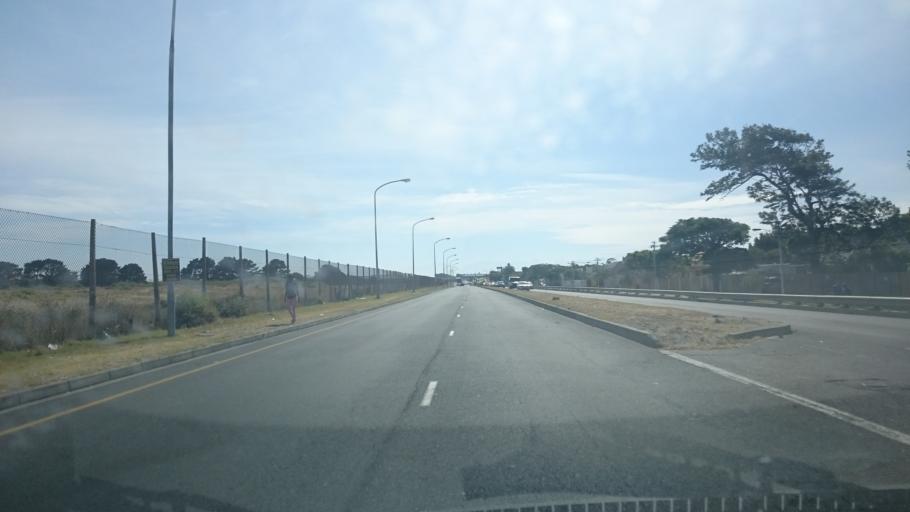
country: ZA
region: Western Cape
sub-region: City of Cape Town
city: Lansdowne
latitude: -34.0129
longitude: 18.4873
